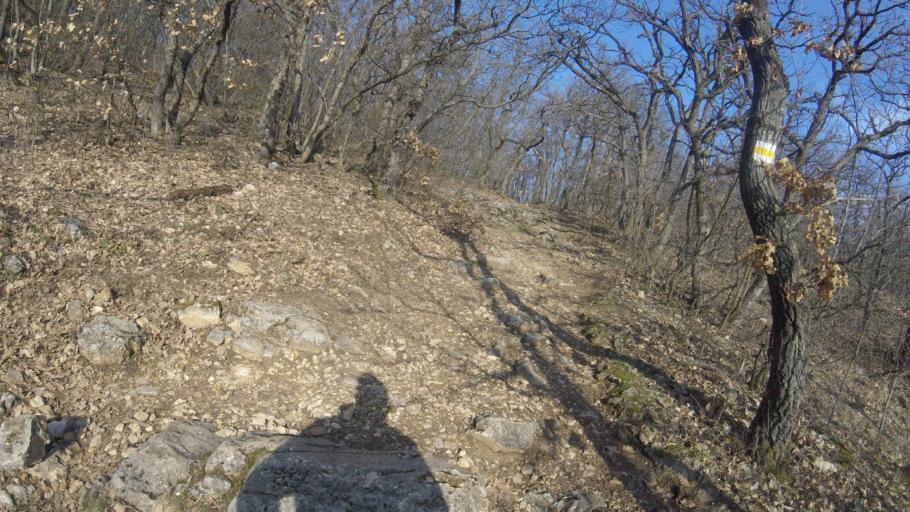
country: HU
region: Pest
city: Csobanka
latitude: 47.6463
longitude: 18.9755
